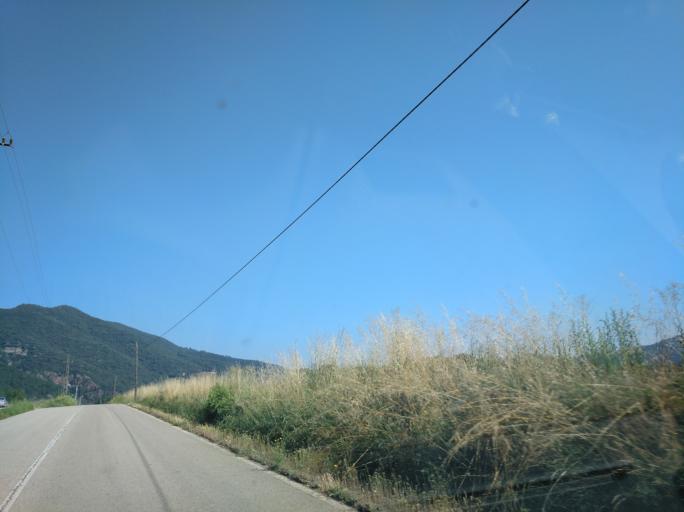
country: ES
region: Catalonia
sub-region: Provincia de Girona
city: la Cellera de Ter
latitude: 41.9758
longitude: 2.6173
